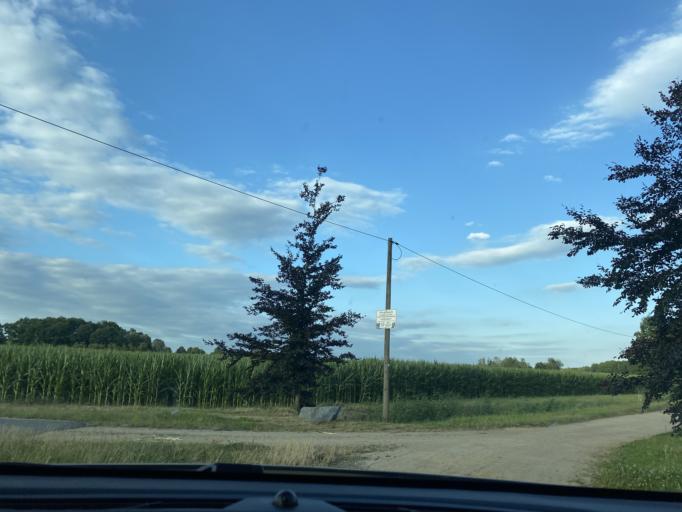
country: DE
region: Saxony
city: Kodersdorf
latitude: 51.2598
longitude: 14.9039
